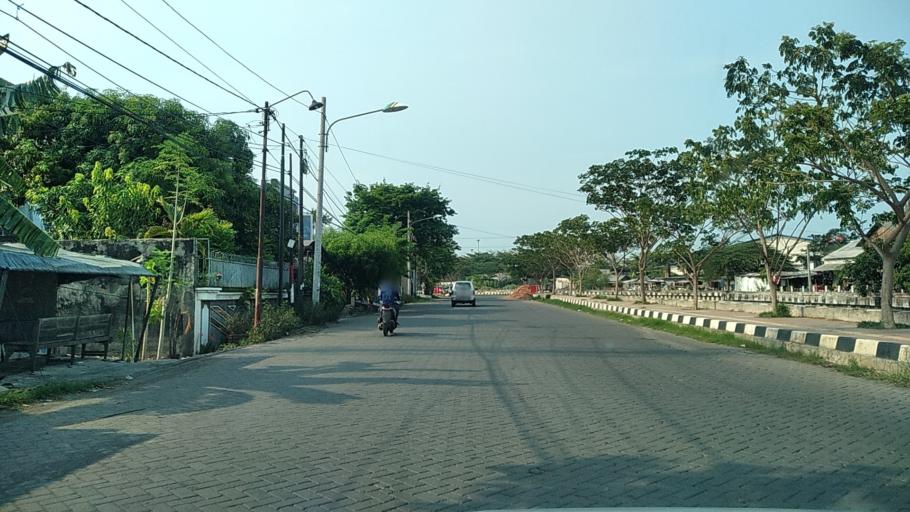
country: ID
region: Central Java
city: Semarang
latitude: -6.9563
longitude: 110.4098
